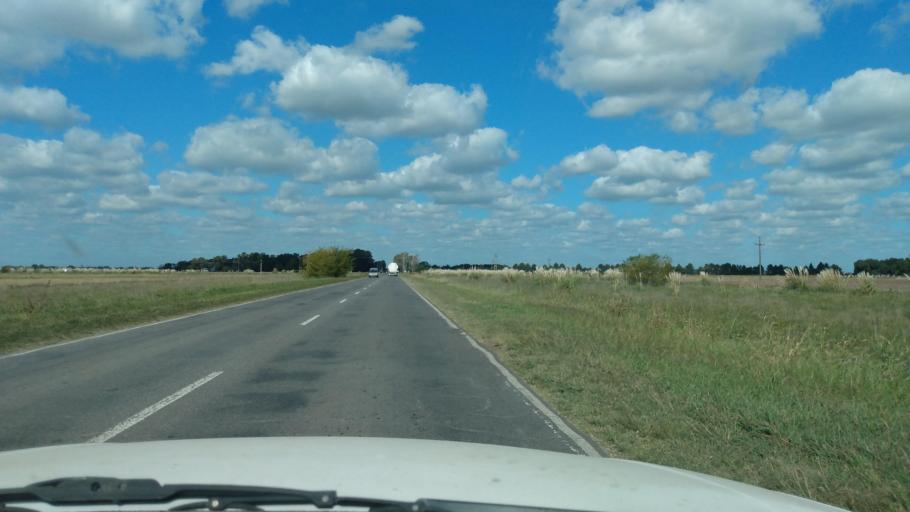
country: AR
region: Buenos Aires
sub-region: Partido de Navarro
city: Navarro
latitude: -34.9823
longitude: -59.3162
